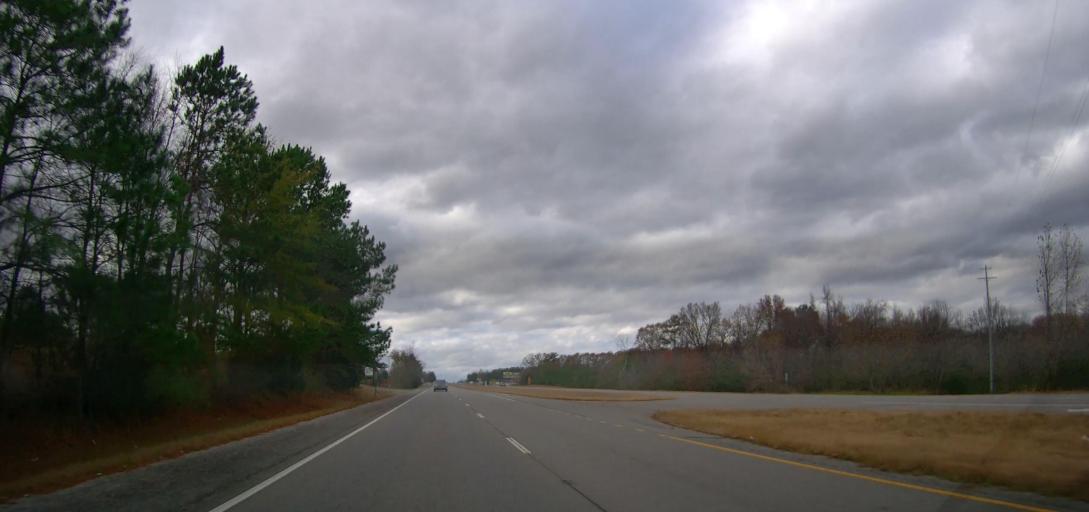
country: US
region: Alabama
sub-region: Lawrence County
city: Town Creek
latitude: 34.5853
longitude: -87.4182
